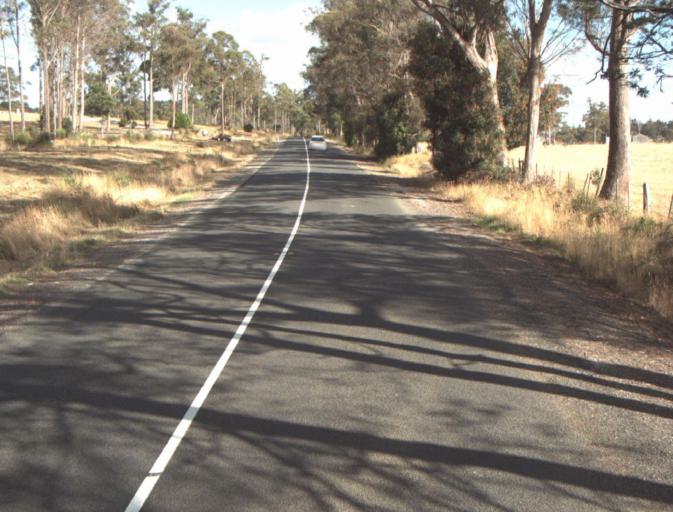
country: AU
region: Tasmania
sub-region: Dorset
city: Bridport
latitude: -41.1159
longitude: 147.2038
